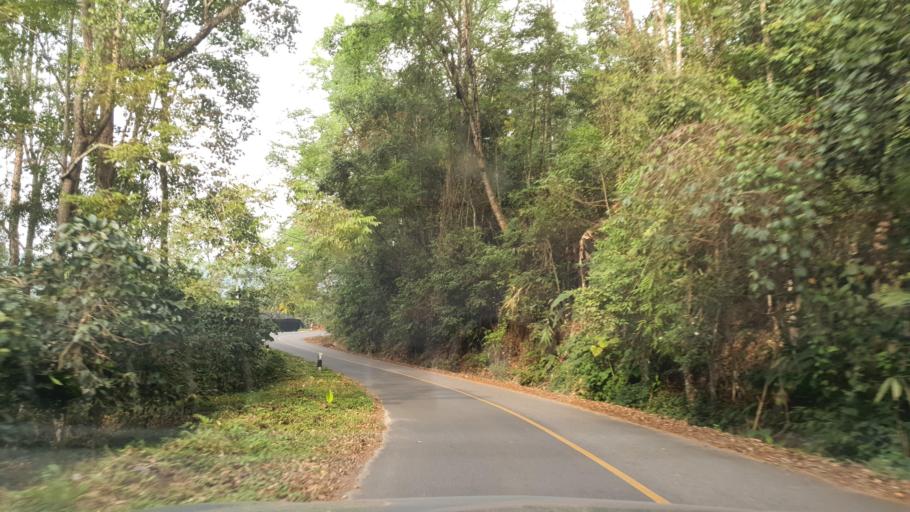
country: TH
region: Chiang Mai
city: Mae On
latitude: 18.9384
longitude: 99.3743
